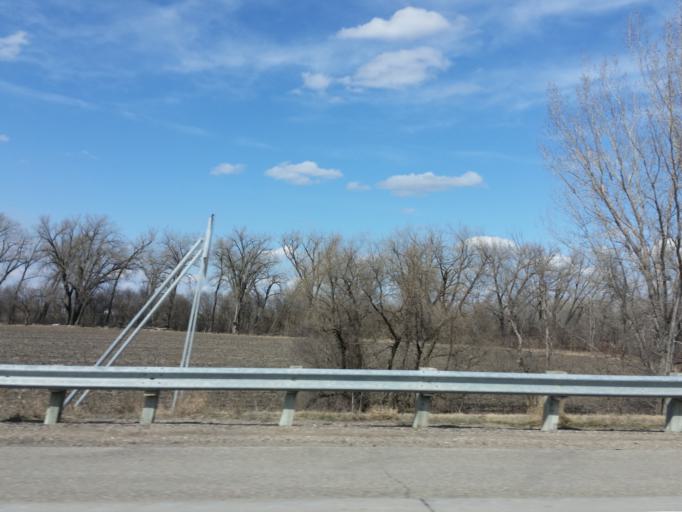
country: US
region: Minnesota
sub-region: Lac qui Parle County
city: Madison
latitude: 44.9359
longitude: -96.1931
